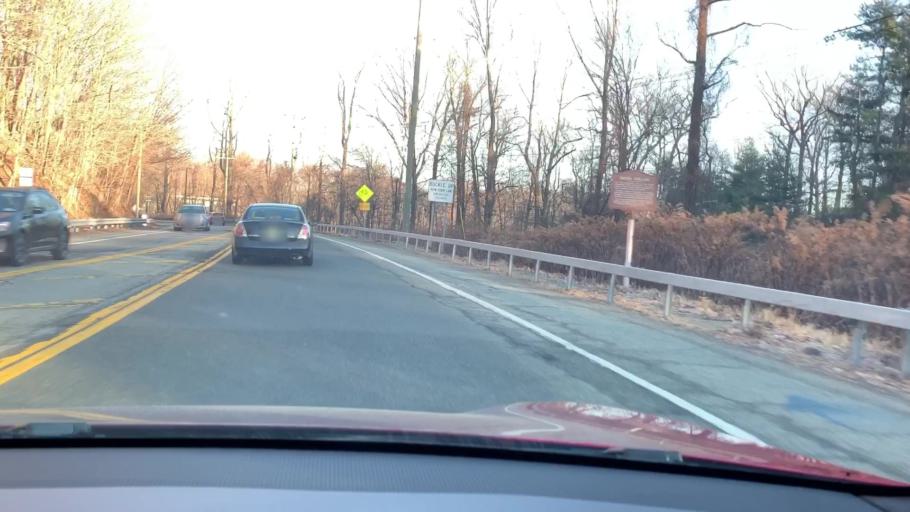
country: US
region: New York
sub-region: Westchester County
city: Hastings-on-Hudson
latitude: 41.0014
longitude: -73.9116
